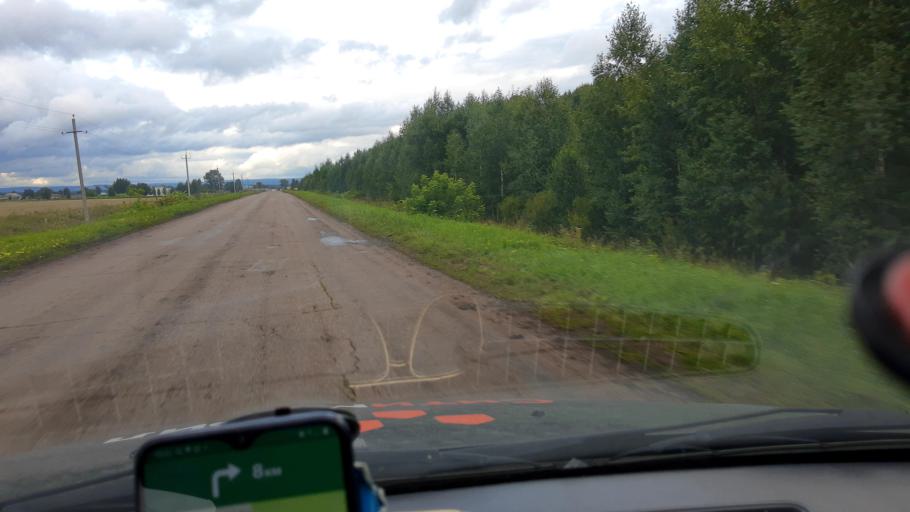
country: RU
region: Bashkortostan
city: Tolbazy
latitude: 53.9876
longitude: 56.2618
